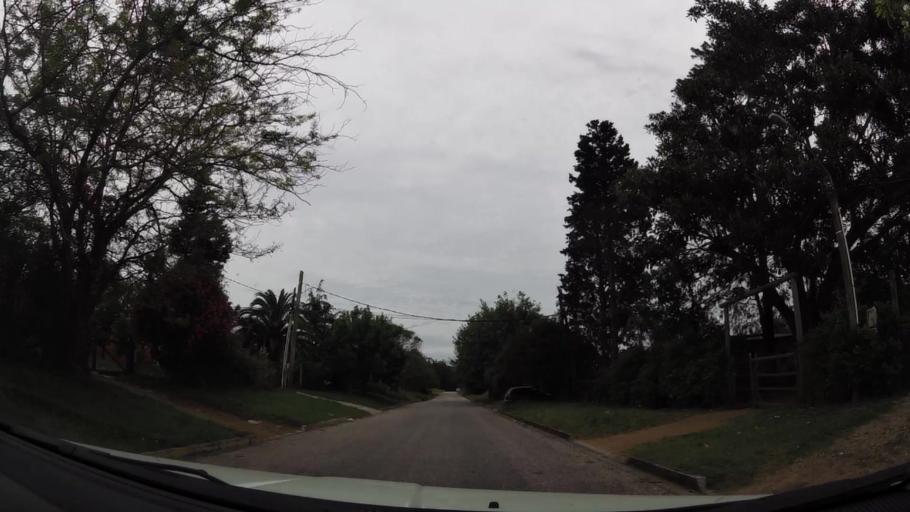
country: UY
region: Maldonado
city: Maldonado
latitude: -34.8806
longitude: -54.9855
